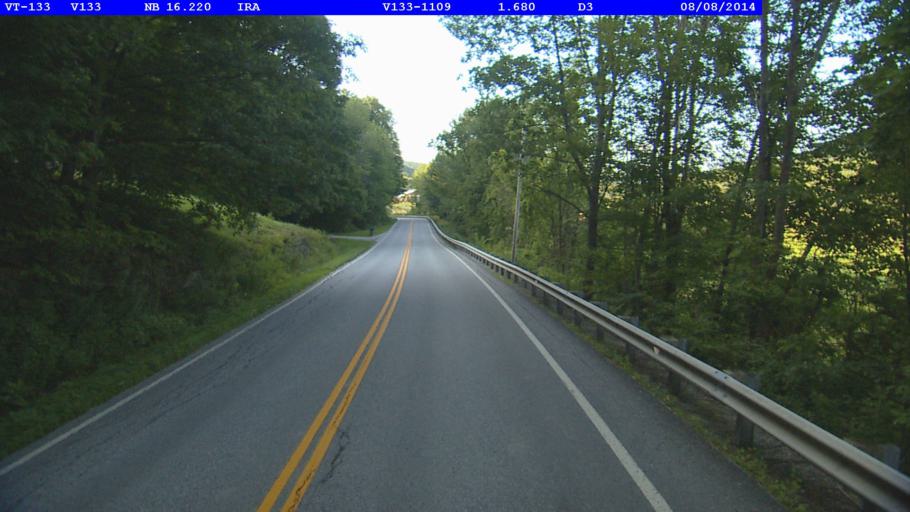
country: US
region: Vermont
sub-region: Rutland County
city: West Rutland
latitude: 43.5179
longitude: -73.0713
